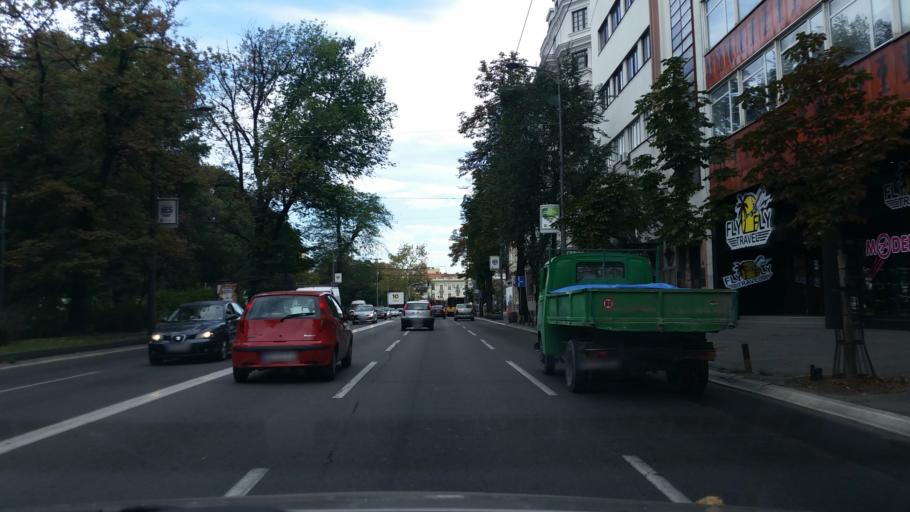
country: RS
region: Central Serbia
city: Belgrade
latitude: 44.8094
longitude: 20.4649
